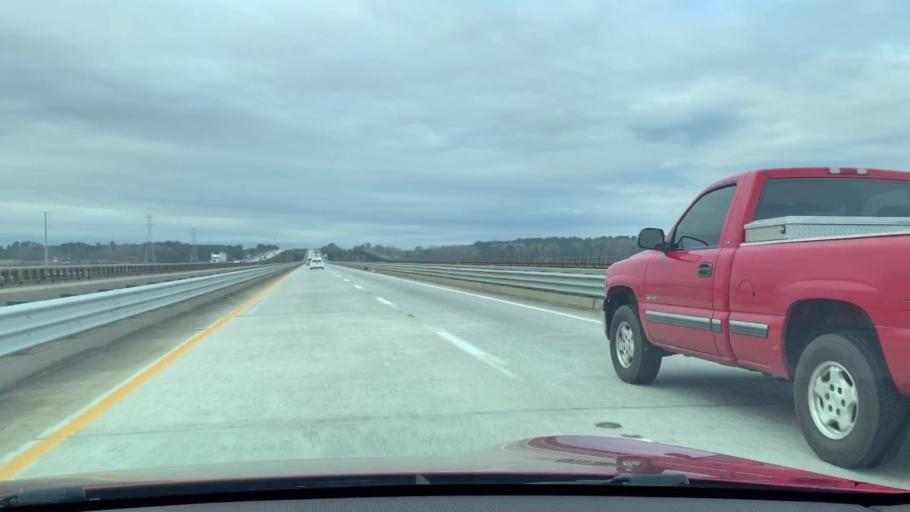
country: US
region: South Carolina
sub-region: Orangeburg County
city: Holly Hill
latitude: 33.5080
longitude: -80.4496
